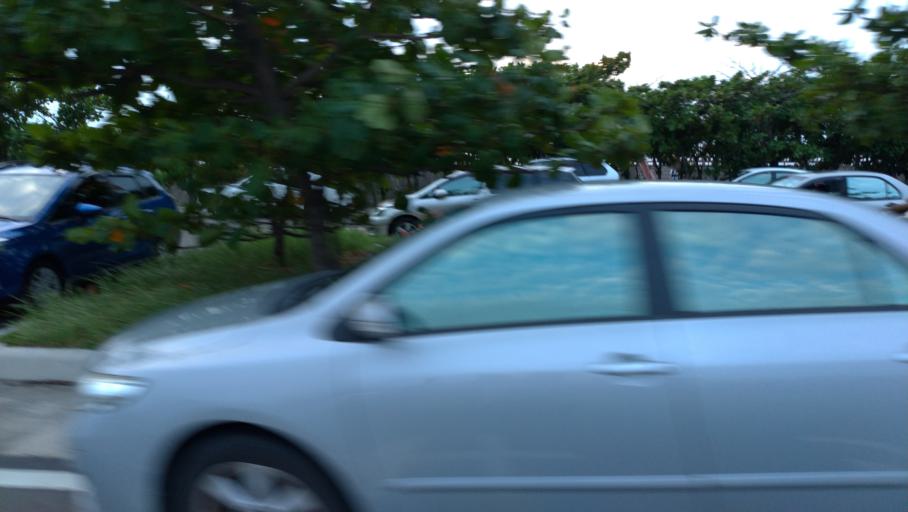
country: TW
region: Taiwan
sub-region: Hsinchu
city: Hsinchu
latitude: 24.7825
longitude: 120.9152
